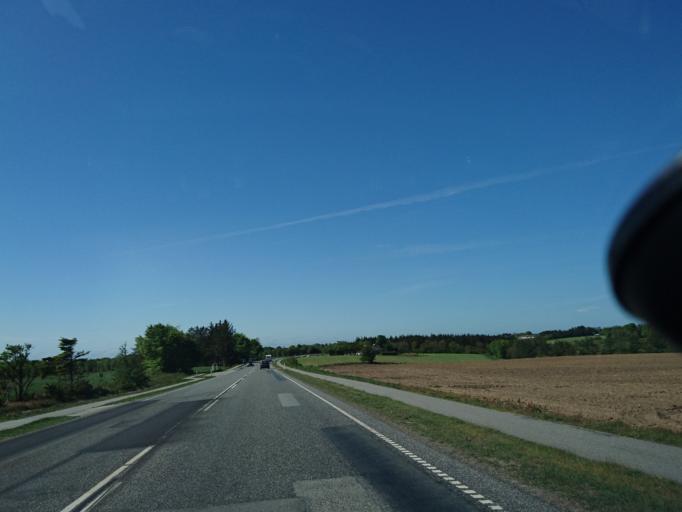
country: DK
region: North Denmark
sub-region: Hjorring Kommune
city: Sindal
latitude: 57.4594
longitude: 10.1455
